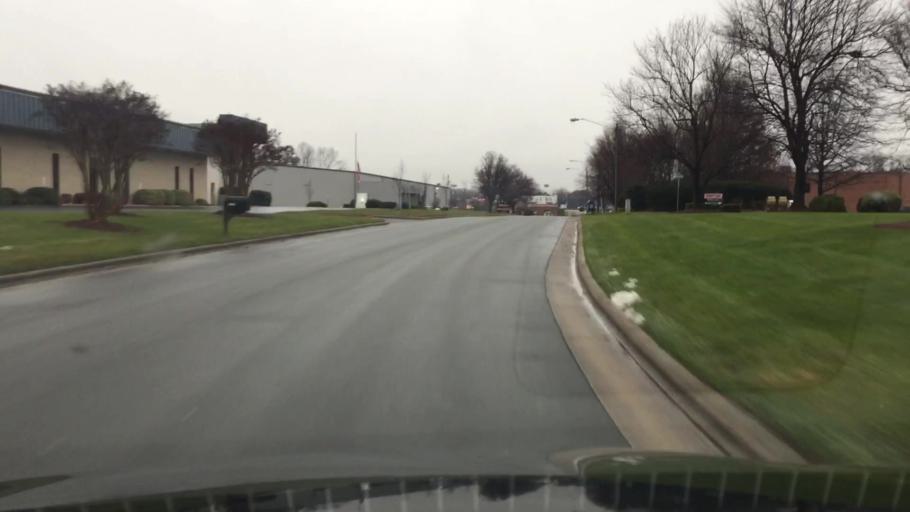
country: US
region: North Carolina
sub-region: Iredell County
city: Mooresville
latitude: 35.5892
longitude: -80.8634
